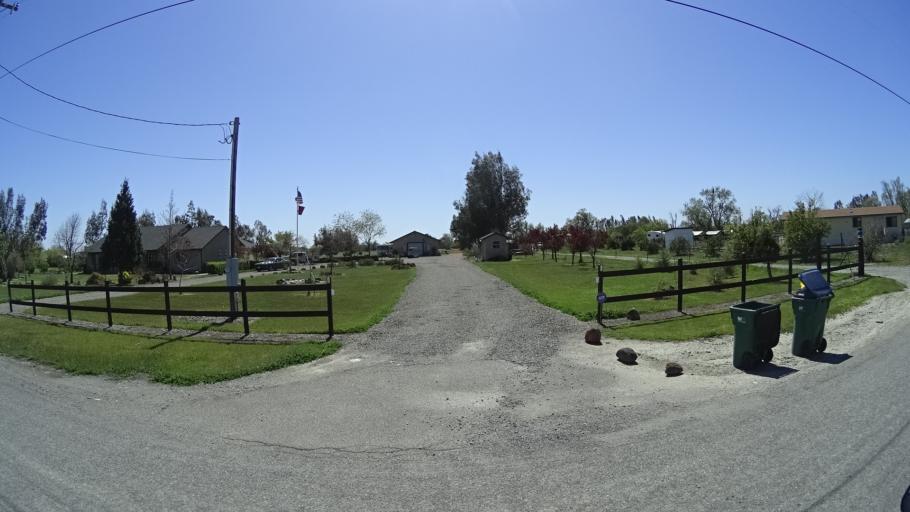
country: US
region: California
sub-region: Glenn County
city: Orland
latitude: 39.7769
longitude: -122.2351
